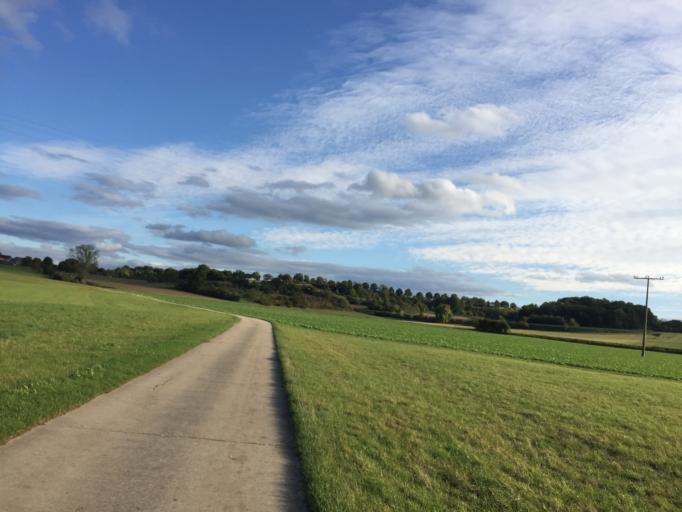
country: DE
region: Hesse
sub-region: Regierungsbezirk Darmstadt
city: Munzenberg
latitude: 50.4555
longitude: 8.7612
